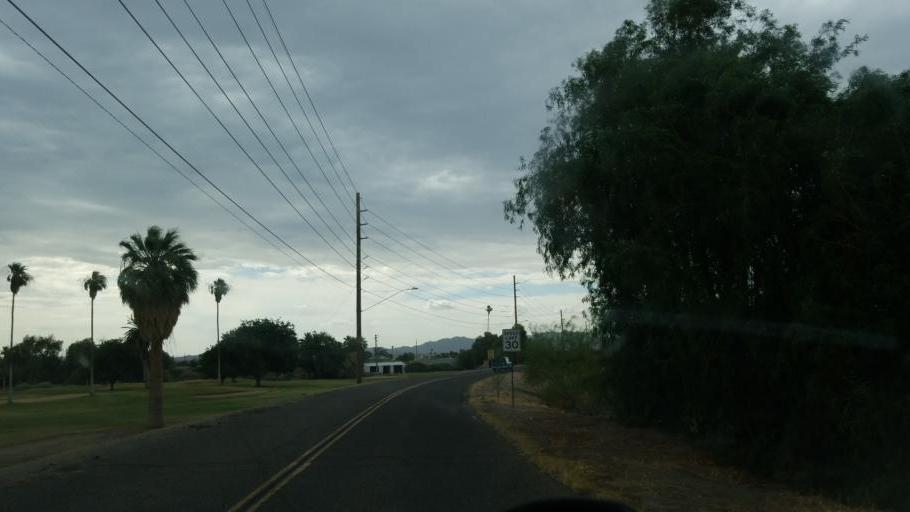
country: US
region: California
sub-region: San Bernardino County
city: Needles
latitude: 34.8454
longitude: -114.6056
